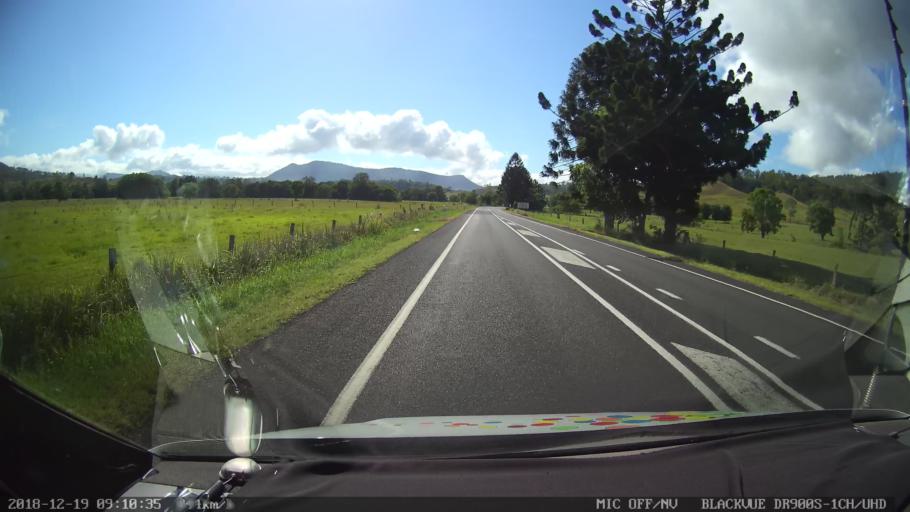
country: AU
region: New South Wales
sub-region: Kyogle
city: Kyogle
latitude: -28.4868
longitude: 152.9309
